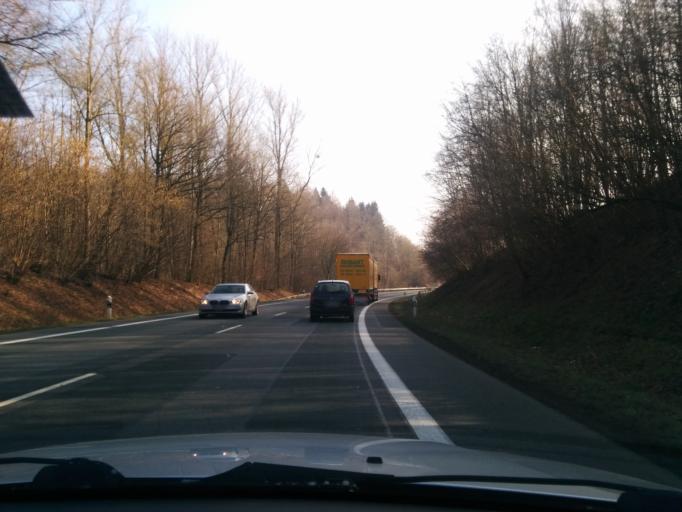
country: DE
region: North Rhine-Westphalia
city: Brakel
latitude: 51.7655
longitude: 9.1668
